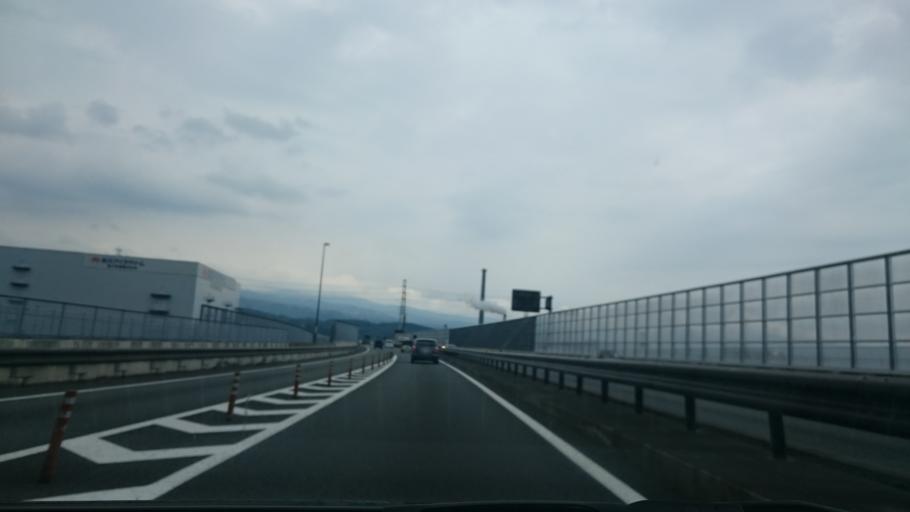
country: JP
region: Shizuoka
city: Mishima
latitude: 35.1496
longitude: 138.8986
